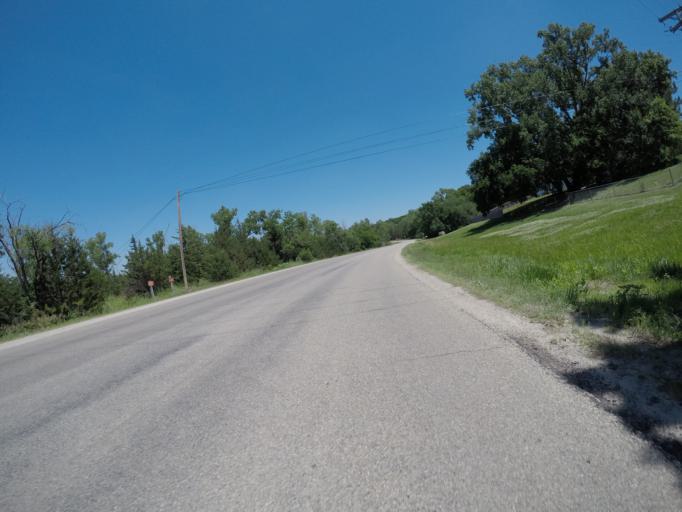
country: US
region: Kansas
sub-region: Geary County
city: Grandview Plaza
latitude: 39.0238
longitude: -96.8031
